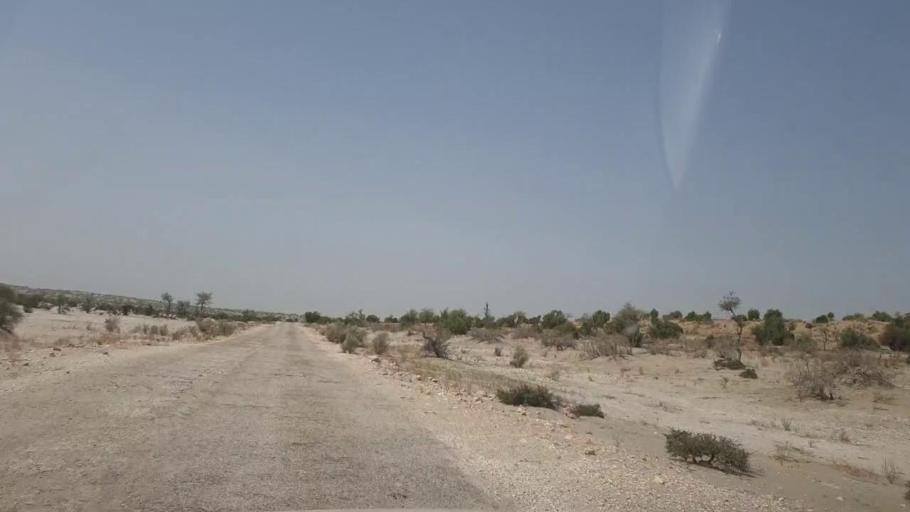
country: PK
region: Sindh
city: Khanpur
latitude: 27.3443
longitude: 69.3180
